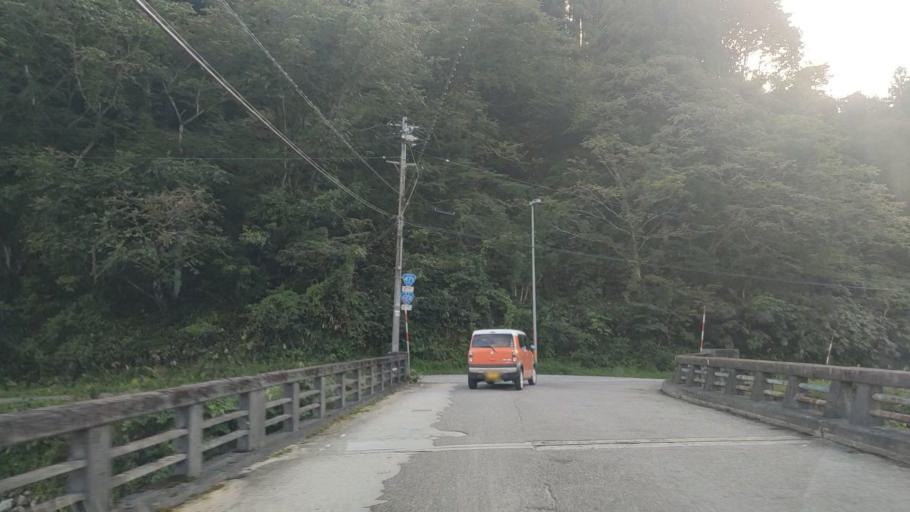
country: JP
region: Toyama
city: Yatsuomachi-higashikumisaka
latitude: 36.4801
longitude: 137.0758
